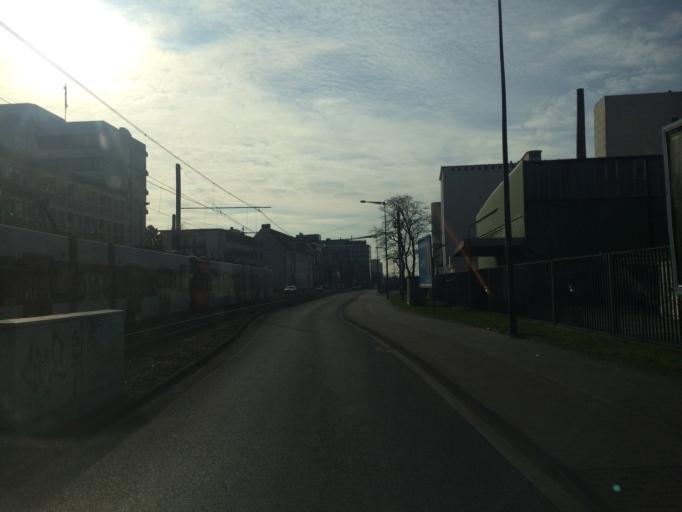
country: DE
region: North Rhine-Westphalia
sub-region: Regierungsbezirk Koln
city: Deutz
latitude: 50.9284
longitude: 6.9751
